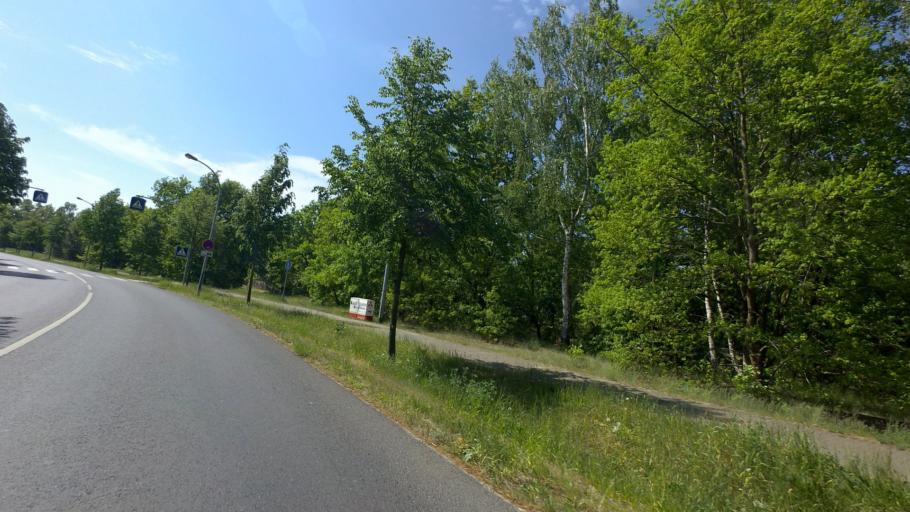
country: DE
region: Brandenburg
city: Oranienburg
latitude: 52.7289
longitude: 13.2395
